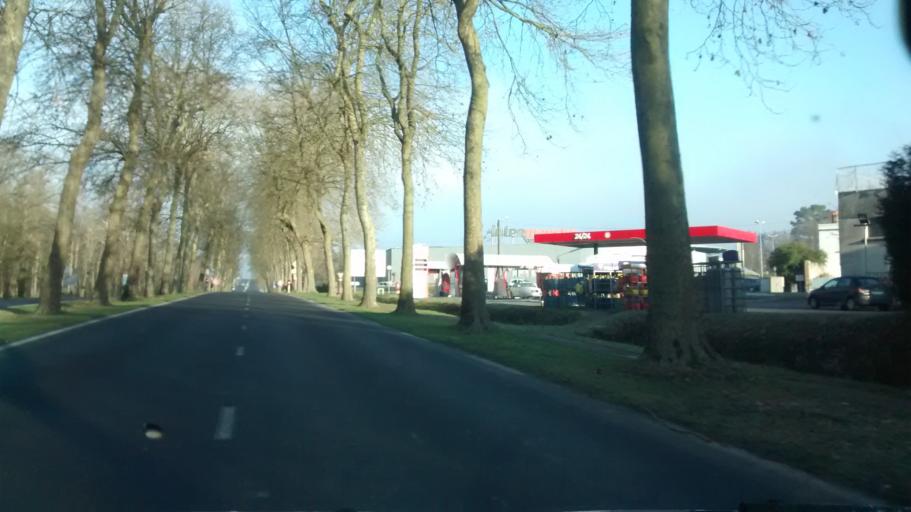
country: FR
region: Centre
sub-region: Departement d'Indre-et-Loire
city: Montbazon
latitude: 47.2917
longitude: 0.7187
